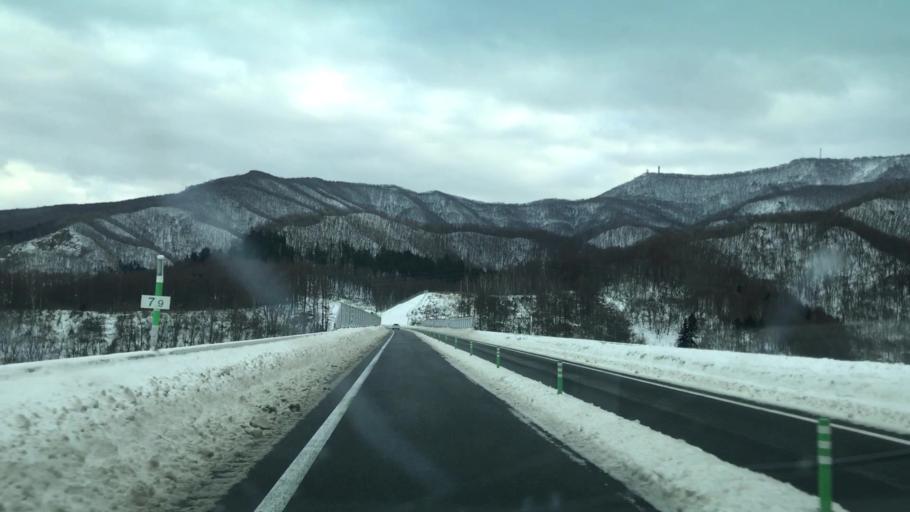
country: JP
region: Hokkaido
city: Otaru
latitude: 43.1658
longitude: 140.9866
